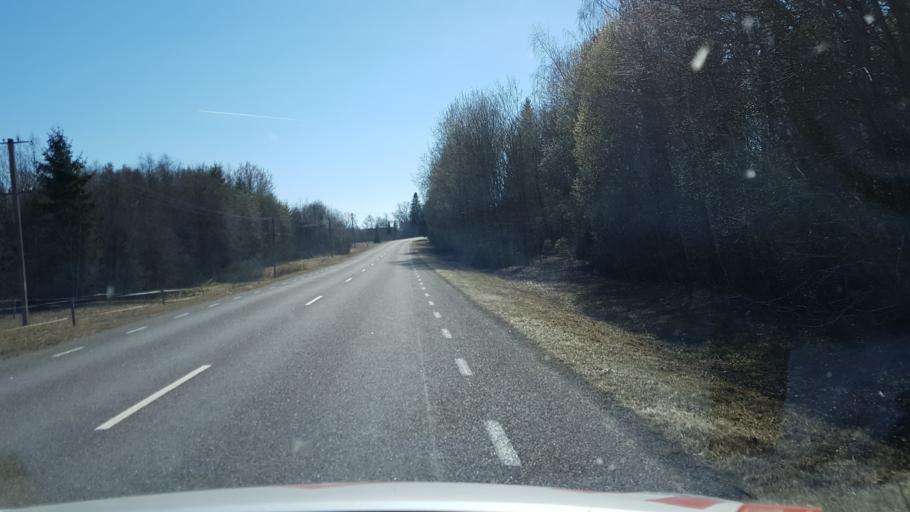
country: EE
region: Jaervamaa
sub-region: Jaerva-Jaani vald
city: Jarva-Jaani
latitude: 59.0662
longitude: 25.9321
